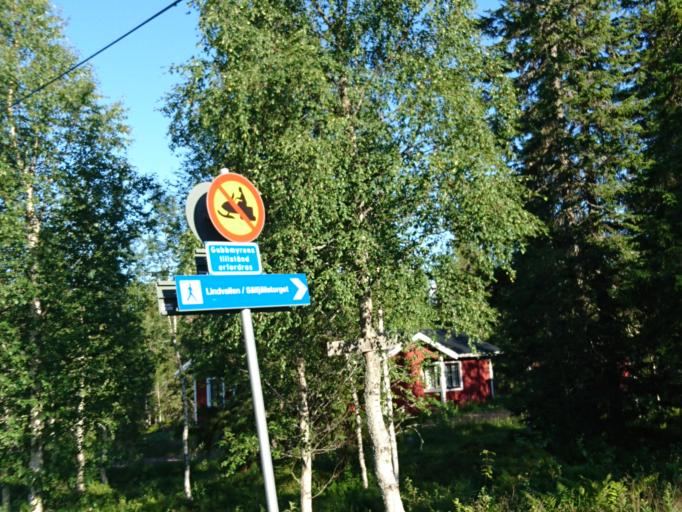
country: SE
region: Dalarna
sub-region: Malung-Saelens kommun
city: Malung
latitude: 61.1707
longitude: 13.1772
